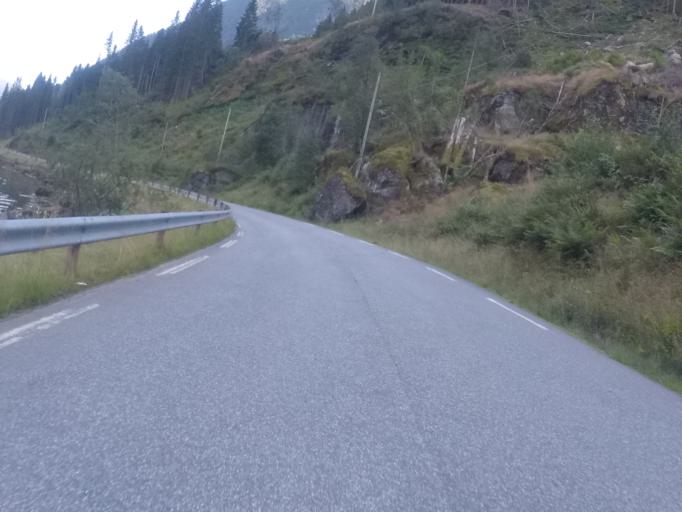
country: NO
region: Sogn og Fjordane
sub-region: Balestrand
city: Balestrand
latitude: 61.2754
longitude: 6.5000
